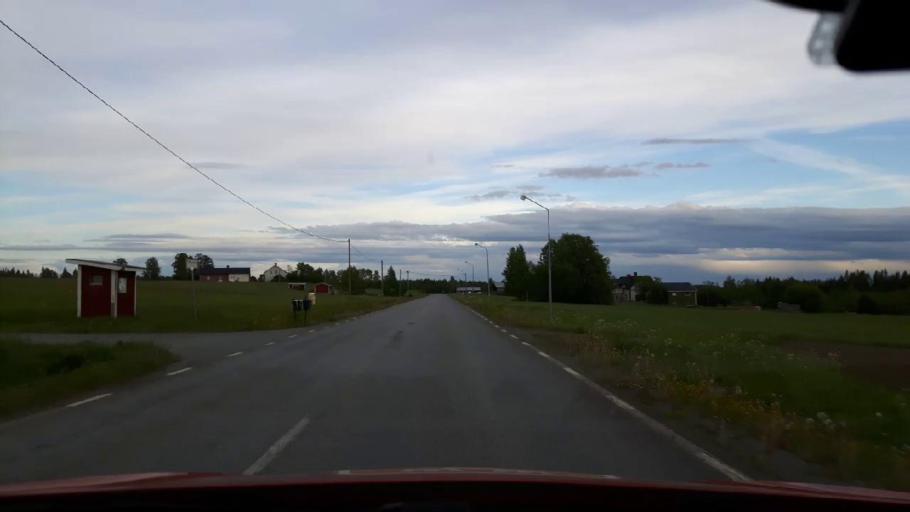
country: SE
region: Jaemtland
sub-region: Bergs Kommun
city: Hoverberg
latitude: 63.0157
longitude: 14.4900
